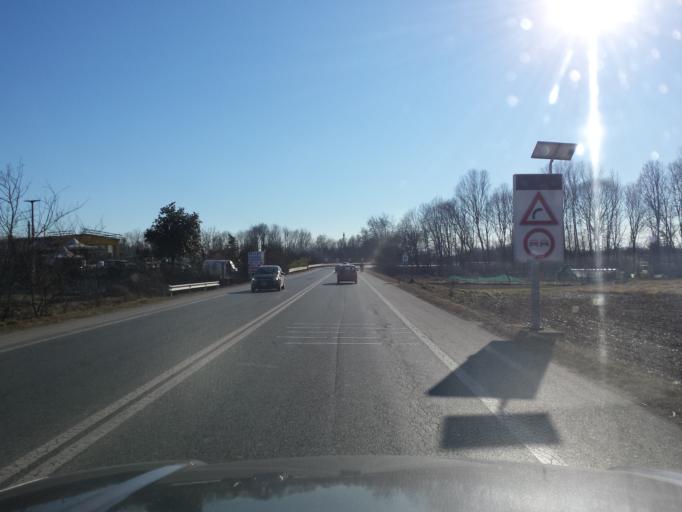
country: IT
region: Piedmont
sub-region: Provincia di Torino
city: Ozegna
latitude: 45.3407
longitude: 7.7404
